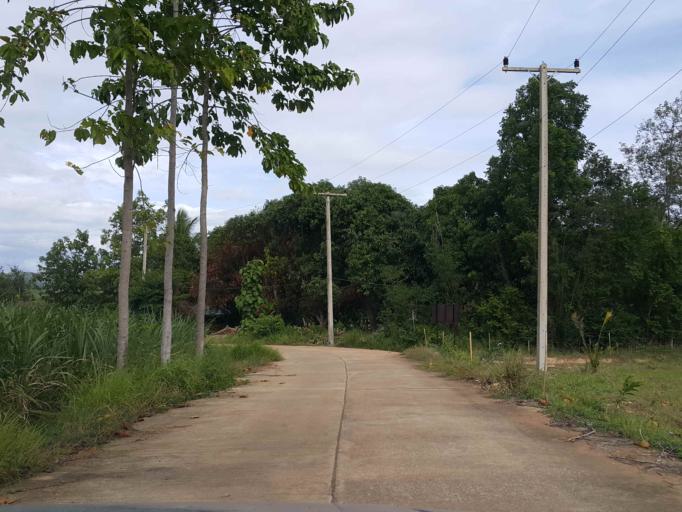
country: TH
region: Sukhothai
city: Thung Saliam
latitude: 17.2304
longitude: 99.5173
